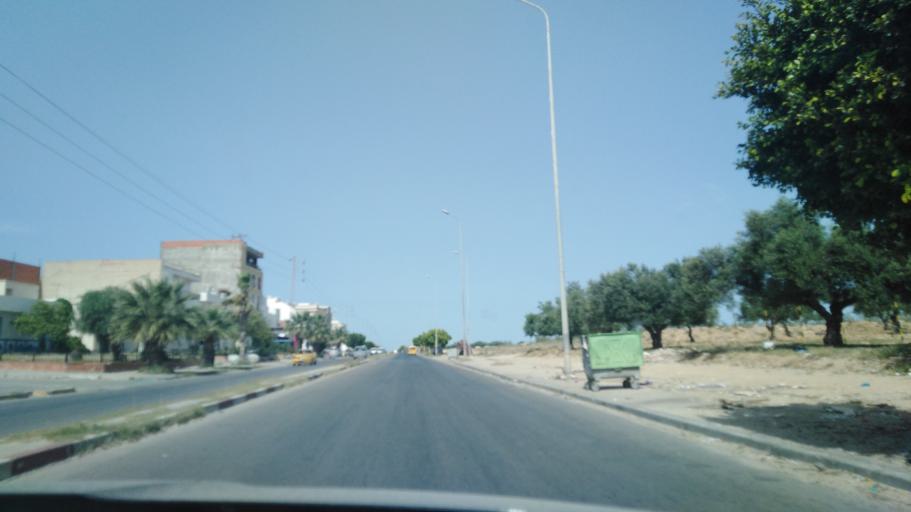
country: TN
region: Susah
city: Sousse
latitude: 35.7904
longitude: 10.5896
